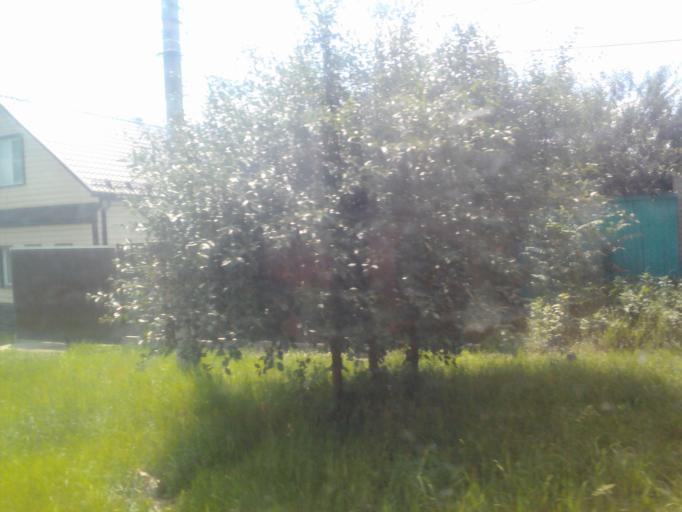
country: RU
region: Kursk
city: Kursk
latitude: 51.7431
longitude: 36.1699
